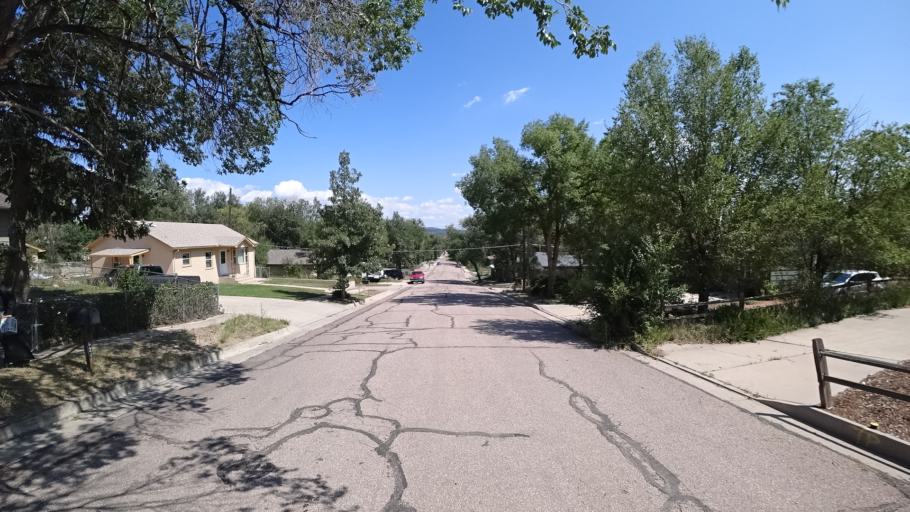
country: US
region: Colorado
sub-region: El Paso County
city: Colorado Springs
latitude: 38.8666
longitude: -104.8401
